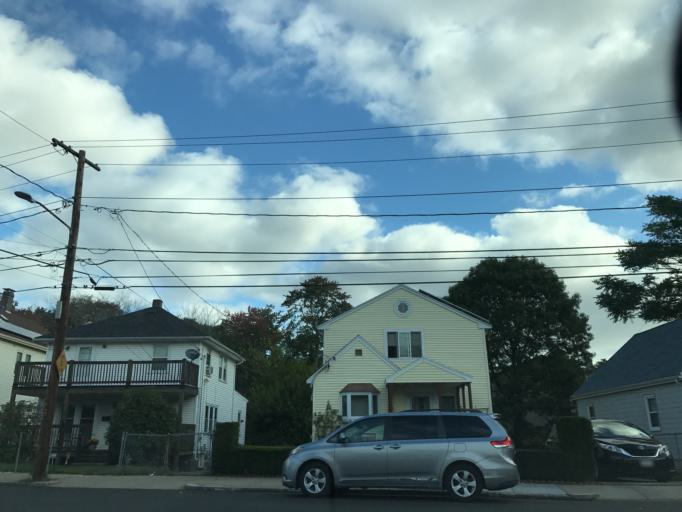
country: US
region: Massachusetts
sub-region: Norfolk County
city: Milton
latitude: 42.2672
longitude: -71.1019
